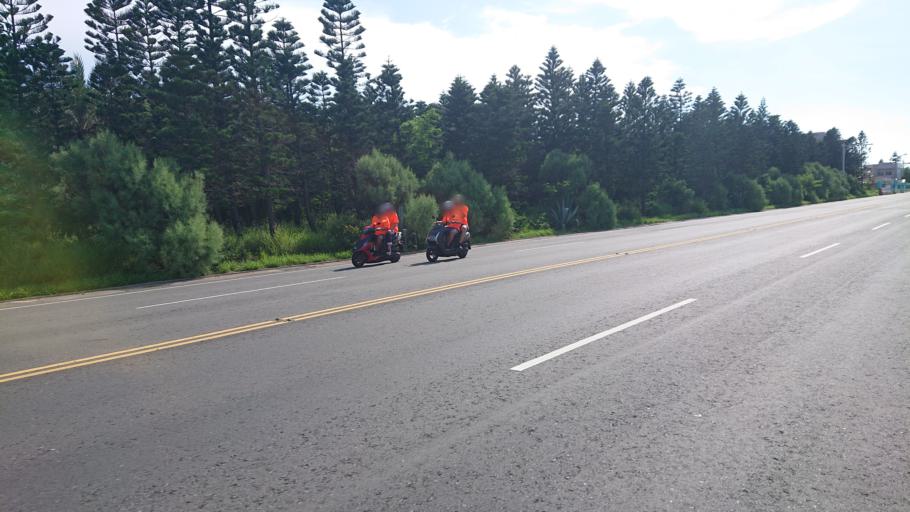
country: TW
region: Taiwan
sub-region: Penghu
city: Ma-kung
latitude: 23.5269
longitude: 119.5921
